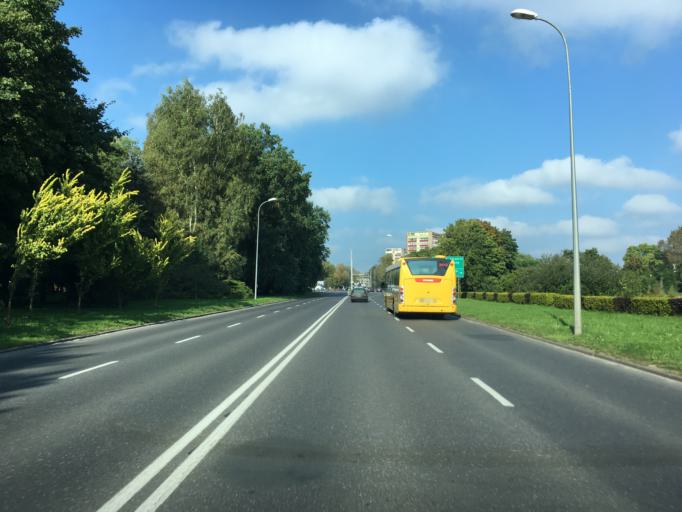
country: PL
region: West Pomeranian Voivodeship
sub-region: Koszalin
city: Koszalin
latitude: 54.1952
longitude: 16.1914
